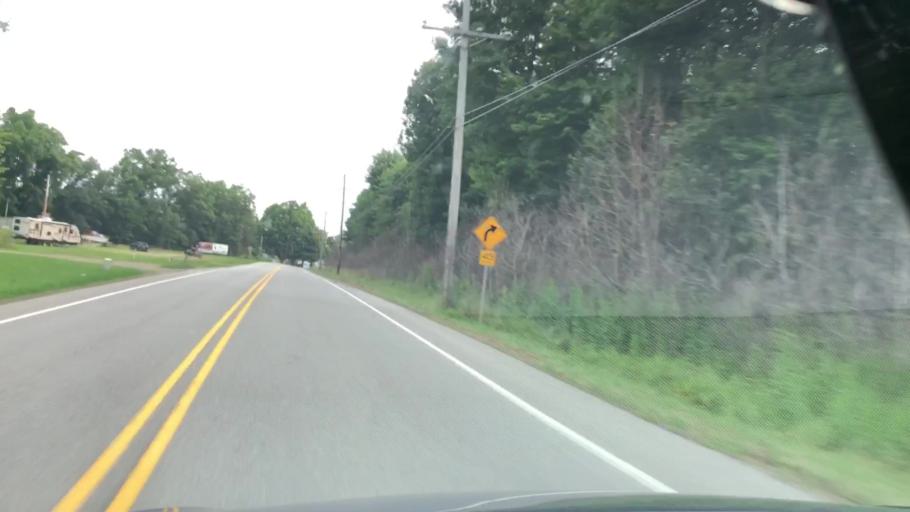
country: US
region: Pennsylvania
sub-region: Crawford County
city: Titusville
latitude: 41.5530
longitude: -79.6993
